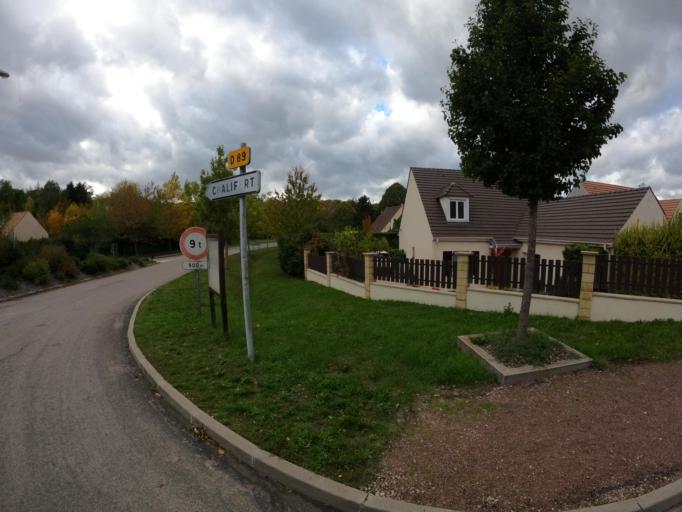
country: FR
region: Ile-de-France
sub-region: Departement de Seine-et-Marne
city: Chalifert
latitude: 48.9034
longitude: 2.7784
